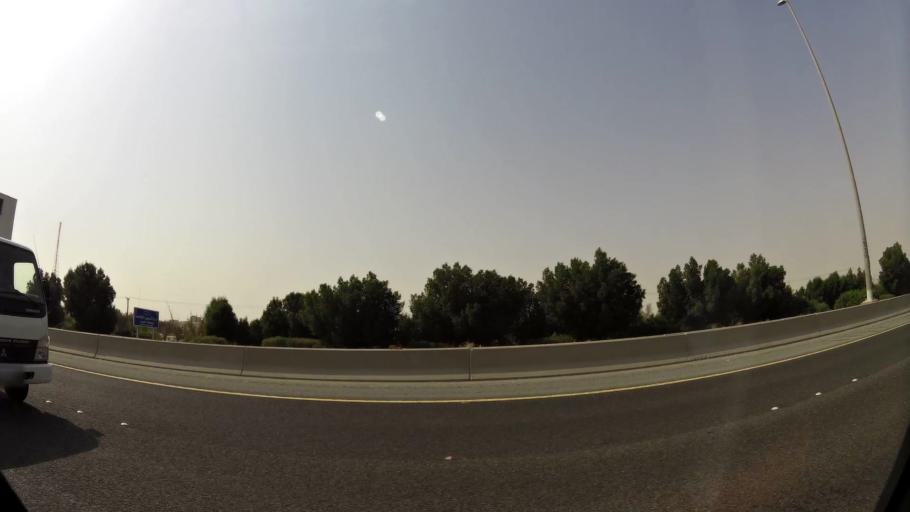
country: KW
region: Muhafazat al Jahra'
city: Al Jahra'
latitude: 29.3641
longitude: 47.6705
